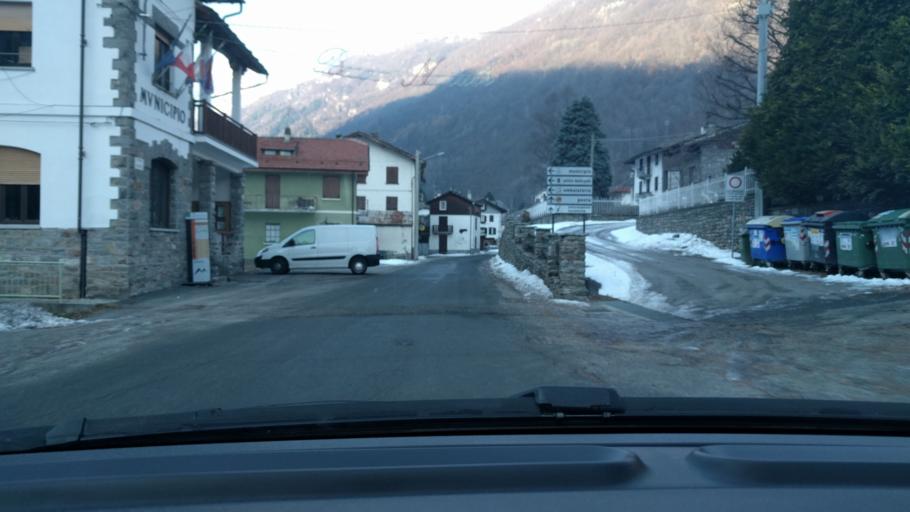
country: IT
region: Piedmont
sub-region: Provincia di Torino
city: Groscavallo
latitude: 45.3690
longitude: 7.2827
